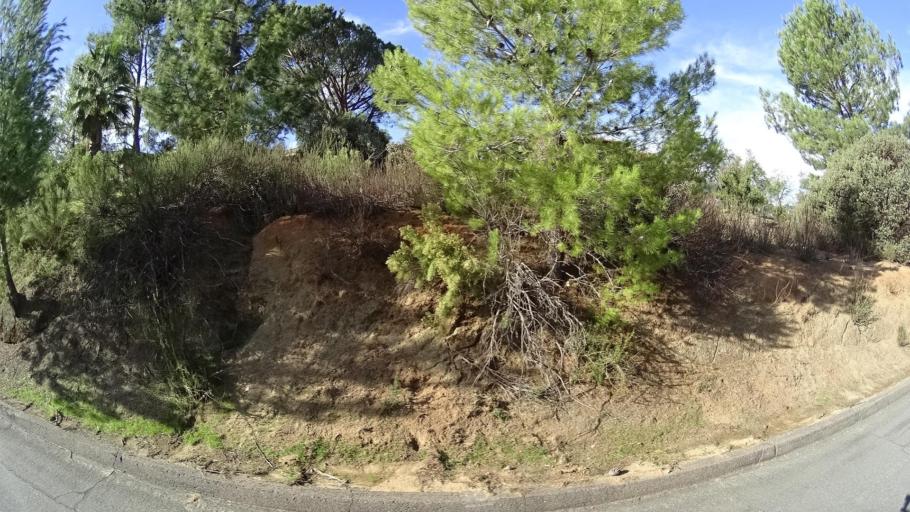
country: US
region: California
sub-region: San Diego County
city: Alpine
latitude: 32.8131
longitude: -116.7326
